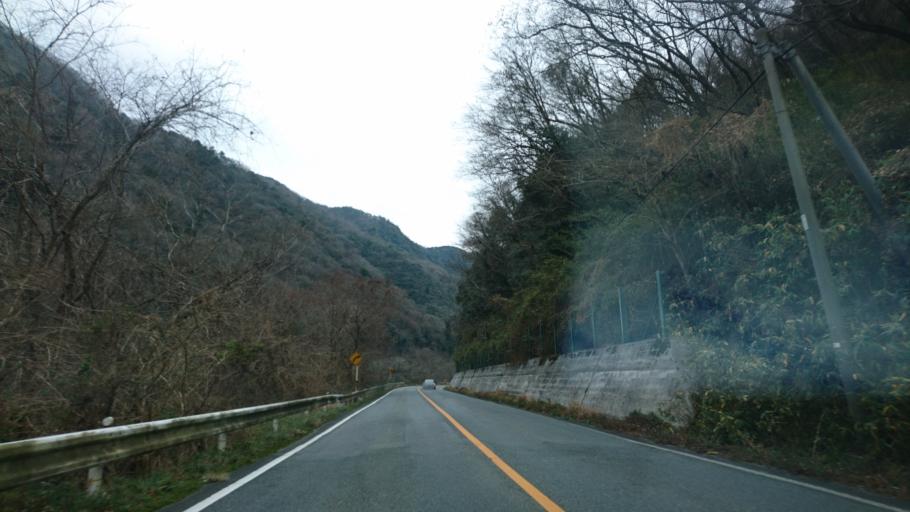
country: JP
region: Okayama
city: Niimi
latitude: 34.8957
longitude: 133.5452
